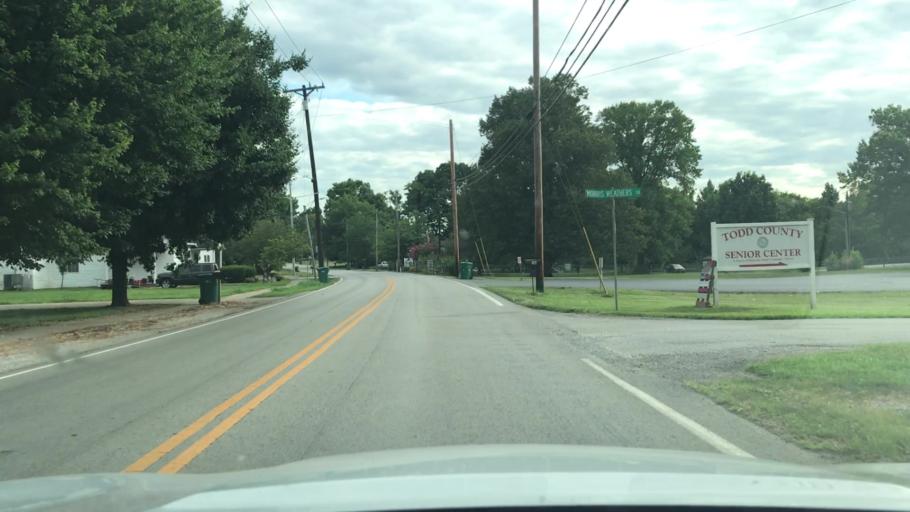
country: US
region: Kentucky
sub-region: Todd County
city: Elkton
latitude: 36.8030
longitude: -87.1562
